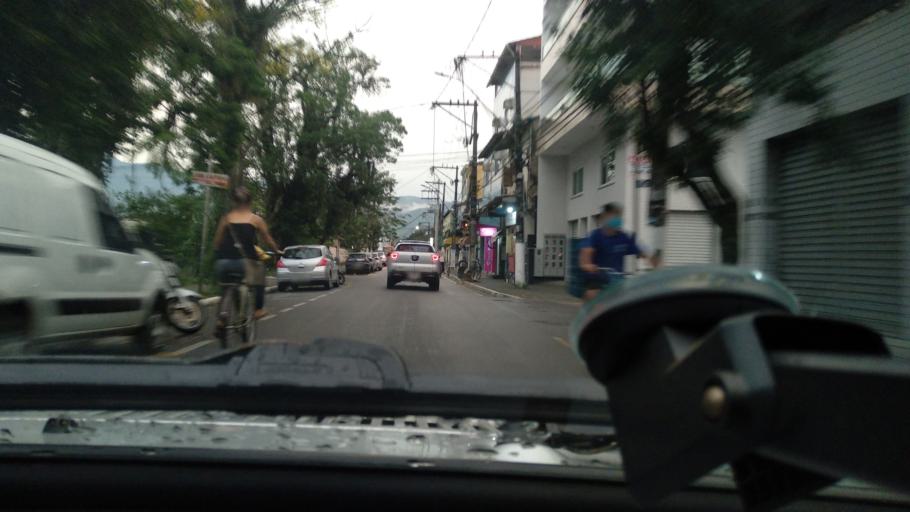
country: BR
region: Rio de Janeiro
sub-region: Angra Dos Reis
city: Angra dos Reis
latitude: -23.0154
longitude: -44.5382
